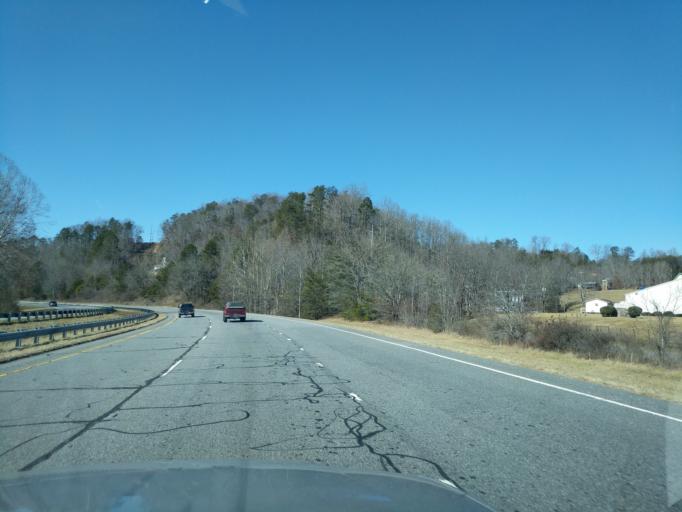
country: US
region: North Carolina
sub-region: Swain County
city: Cherokee
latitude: 35.4218
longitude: -83.3364
